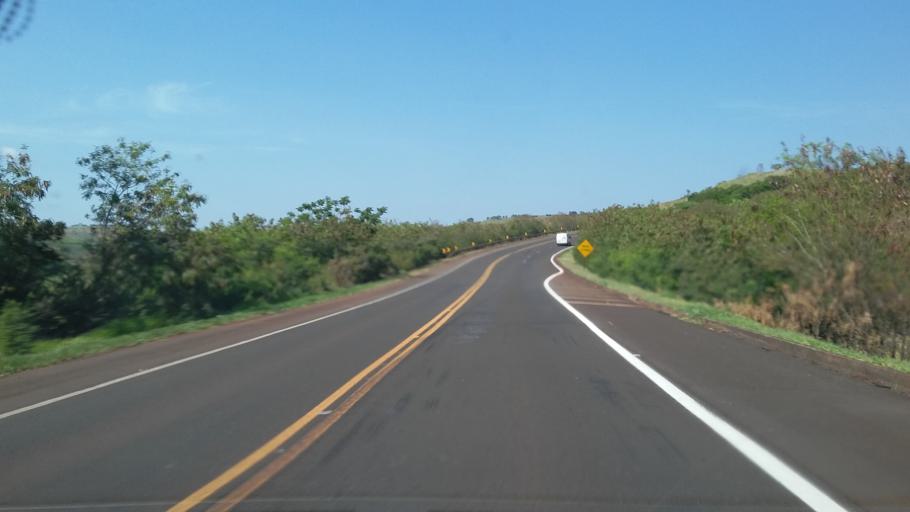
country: BR
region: Parana
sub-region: Bandeirantes
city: Bandeirantes
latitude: -23.1379
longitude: -50.3806
